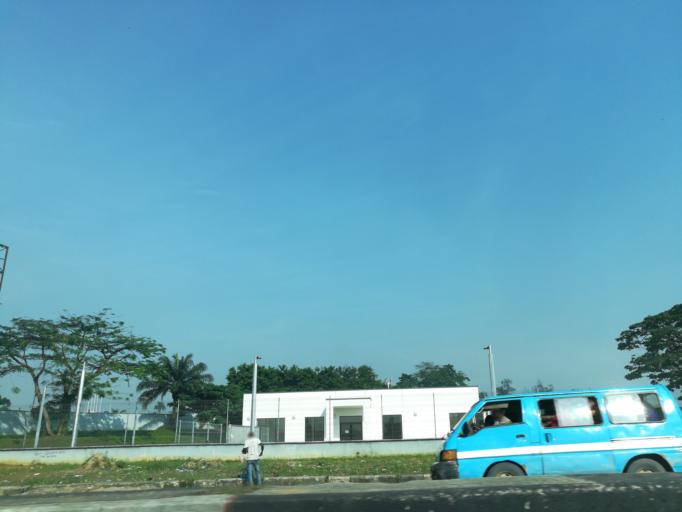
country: NG
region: Rivers
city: Port Harcourt
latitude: 4.8353
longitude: 7.0095
